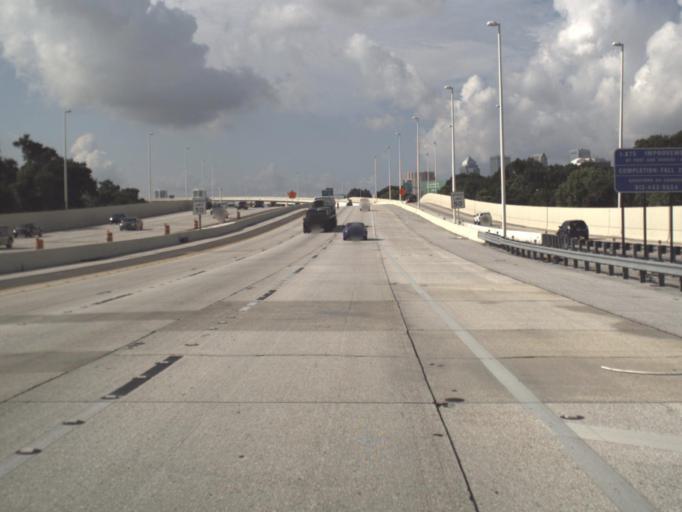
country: US
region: Florida
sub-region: Hillsborough County
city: Tampa
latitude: 27.9700
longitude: -82.4536
